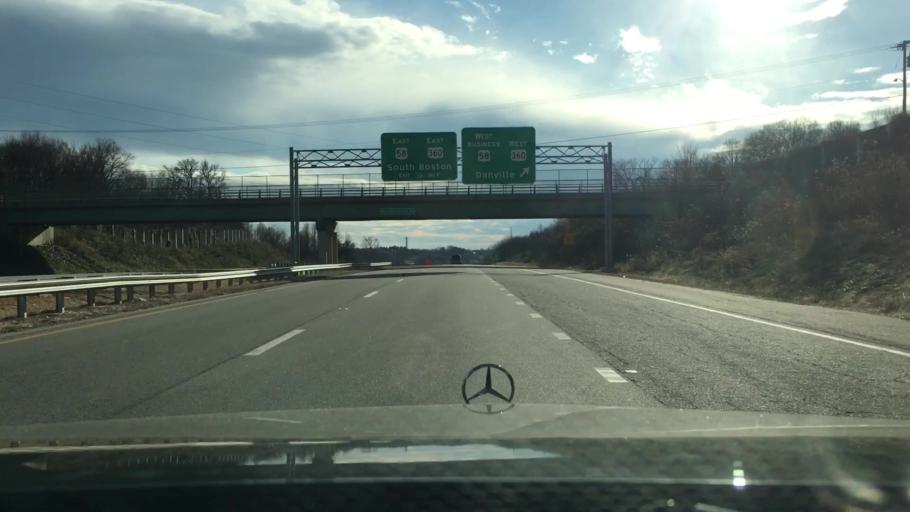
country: US
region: Virginia
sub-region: City of Danville
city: Danville
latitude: 36.5891
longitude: -79.3572
